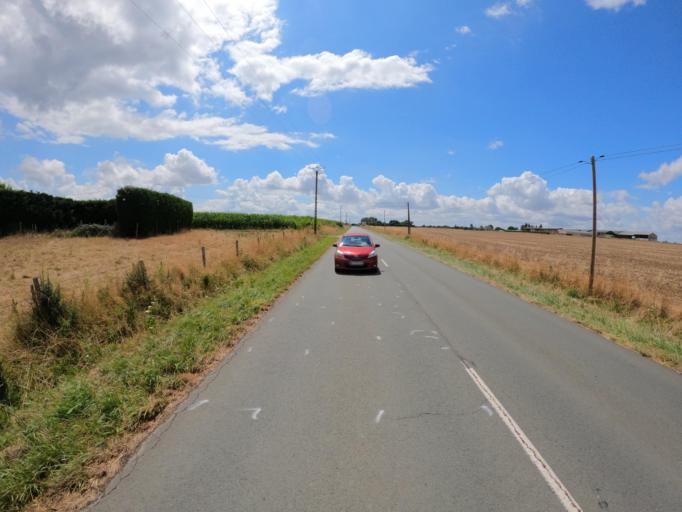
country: FR
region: Pays de la Loire
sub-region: Departement de Maine-et-Loire
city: Champigne
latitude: 47.7052
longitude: -0.5382
